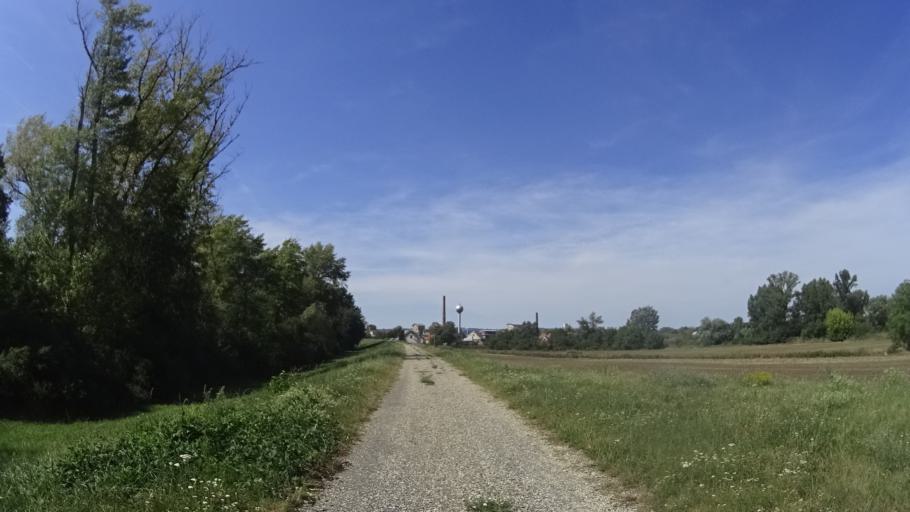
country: AT
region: Lower Austria
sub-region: Politischer Bezirk Ganserndorf
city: Angern an der March
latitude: 48.3754
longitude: 16.8439
